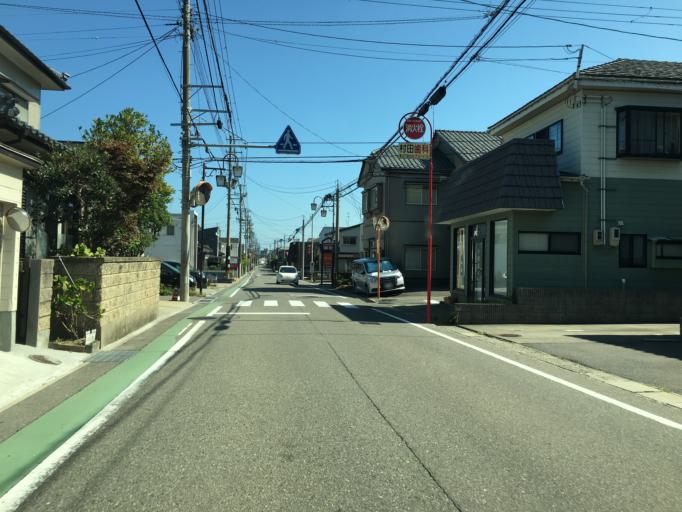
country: JP
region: Niigata
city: Niigata-shi
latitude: 37.9016
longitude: 138.9994
